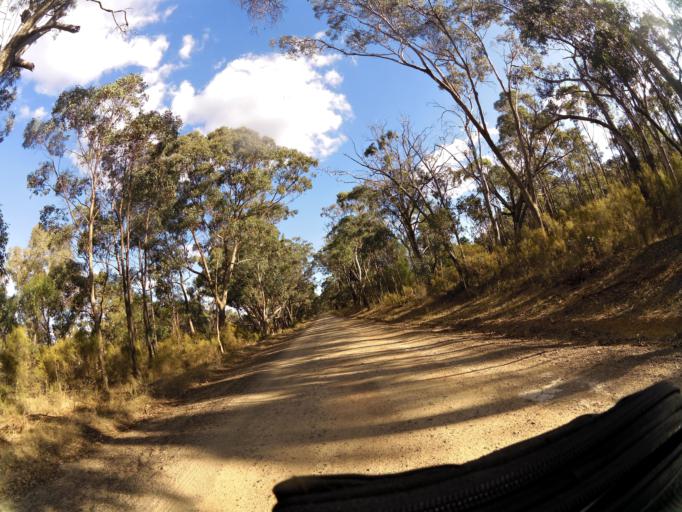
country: AU
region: Victoria
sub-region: Greater Bendigo
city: Kennington
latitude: -37.0118
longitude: 144.8090
